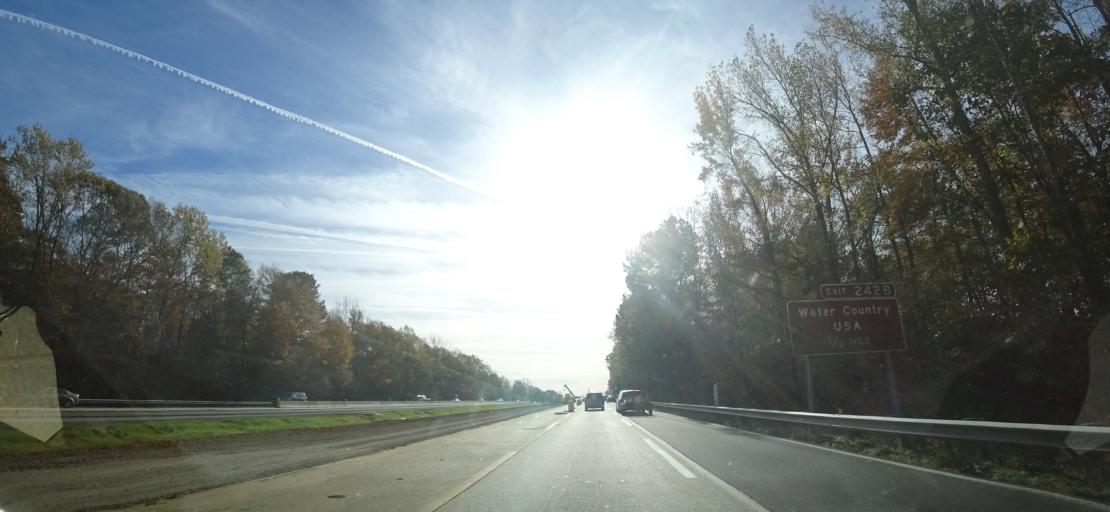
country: US
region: Virginia
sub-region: City of Williamsburg
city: Williamsburg
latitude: 37.2635
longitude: -76.6506
